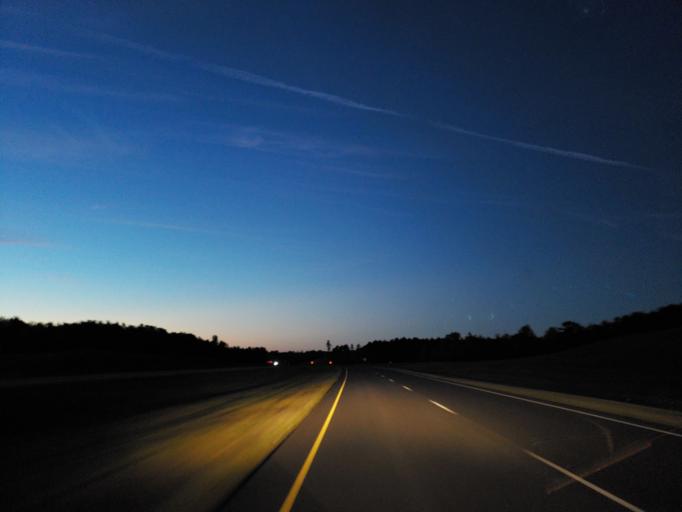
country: US
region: Mississippi
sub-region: Clarke County
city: Quitman
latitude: 32.0599
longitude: -88.6784
